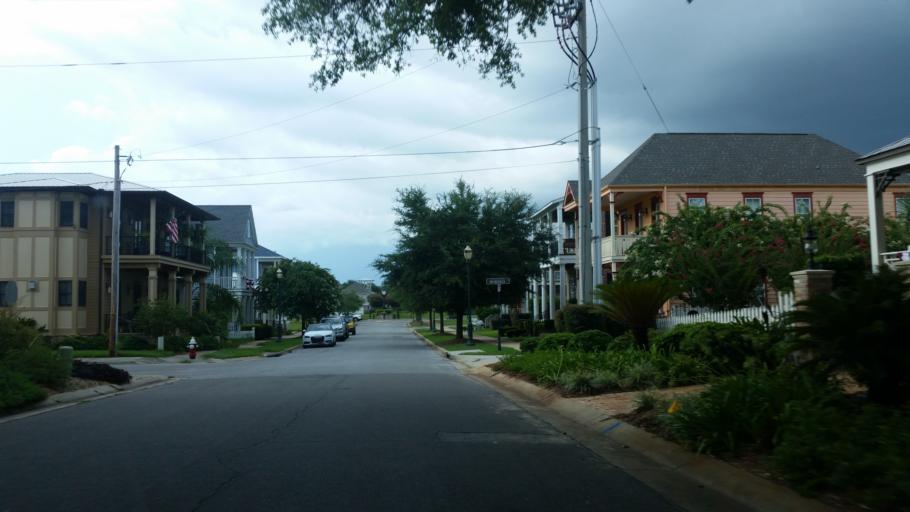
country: US
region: Florida
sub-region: Escambia County
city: Pensacola
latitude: 30.4115
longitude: -87.2062
